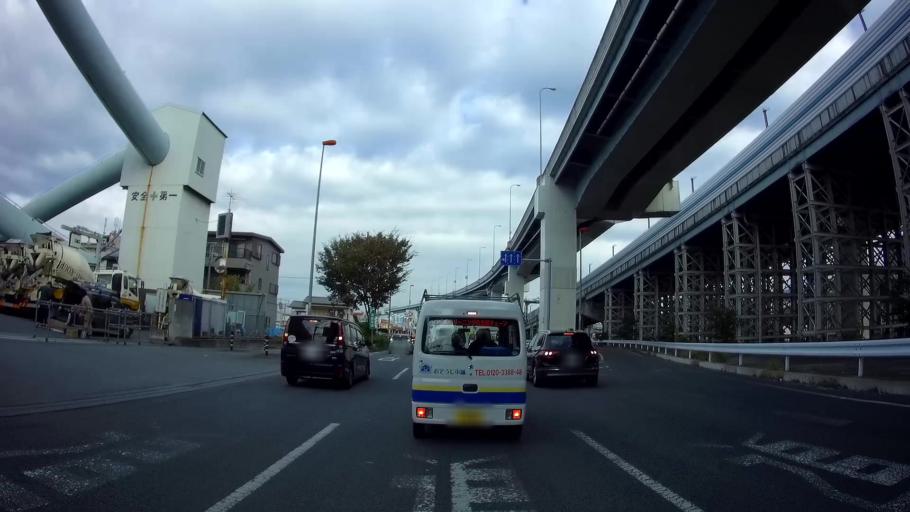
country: JP
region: Saitama
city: Yono
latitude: 35.8878
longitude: 139.6136
